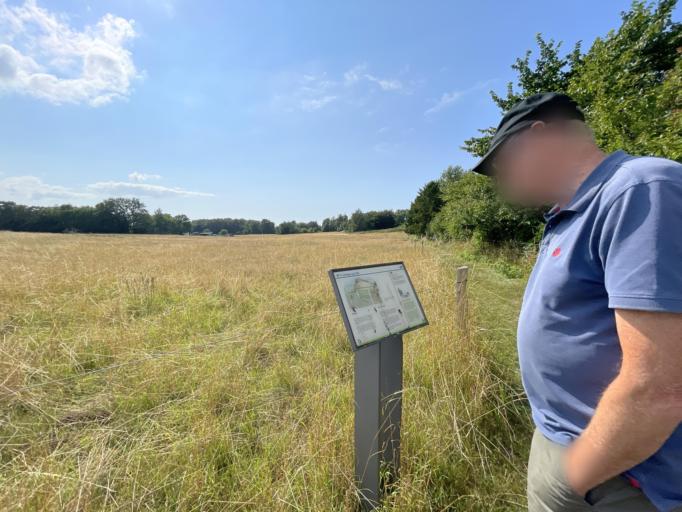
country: DK
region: Capital Region
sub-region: Gribskov Kommune
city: Helsinge
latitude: 56.0914
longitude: 12.1831
